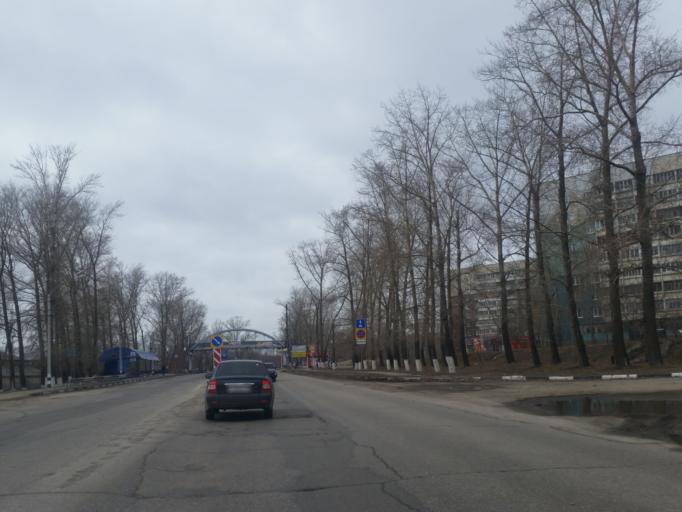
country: RU
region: Ulyanovsk
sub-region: Ulyanovskiy Rayon
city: Ulyanovsk
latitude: 54.3212
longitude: 48.4785
